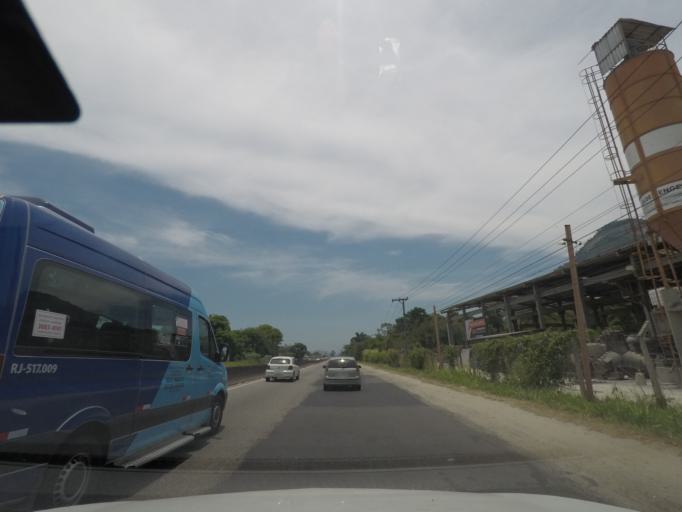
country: BR
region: Rio de Janeiro
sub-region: Marica
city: Marica
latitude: -22.9341
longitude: -42.8971
